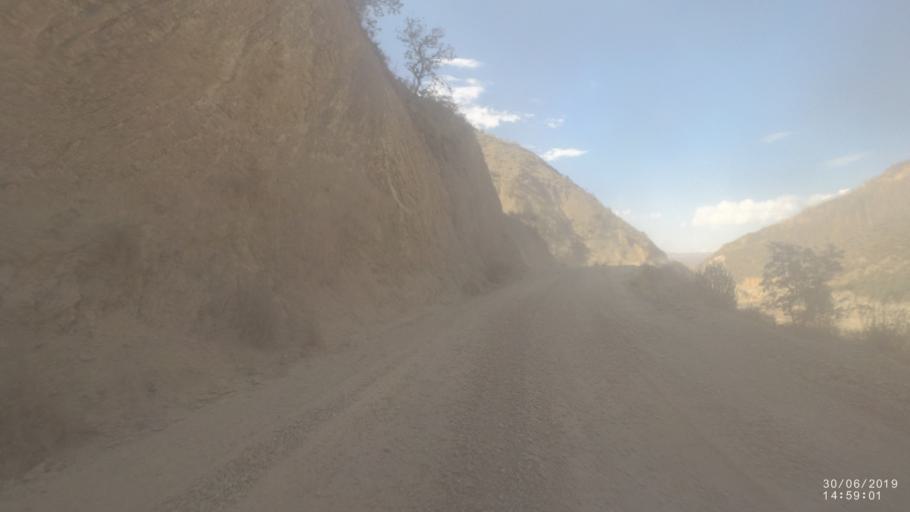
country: BO
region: Cochabamba
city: Irpa Irpa
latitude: -17.7376
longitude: -66.3468
